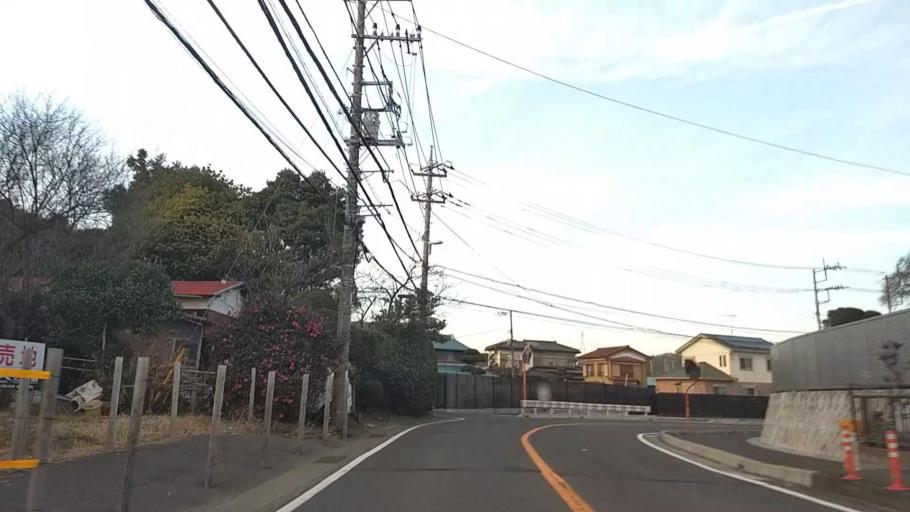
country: JP
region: Kanagawa
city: Atsugi
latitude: 35.4488
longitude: 139.3282
